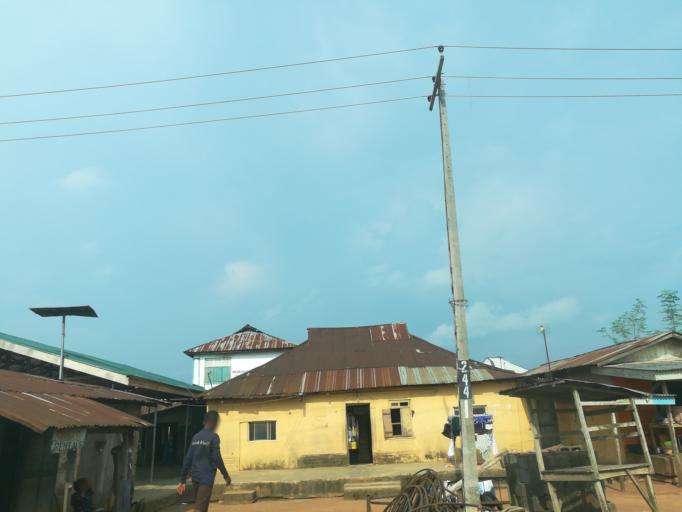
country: NG
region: Lagos
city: Ikorodu
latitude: 6.6665
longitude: 3.6714
